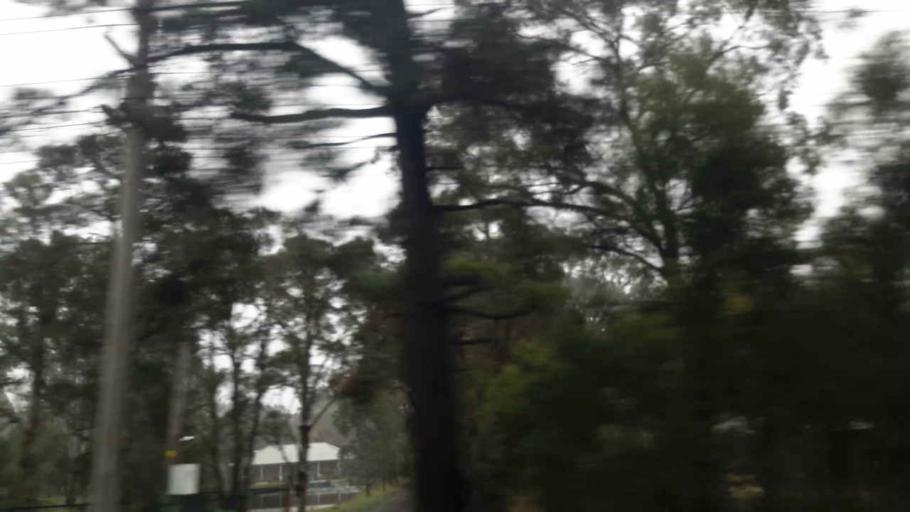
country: AU
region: New South Wales
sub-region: Hawkesbury
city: South Windsor
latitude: -33.6482
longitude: 150.7787
